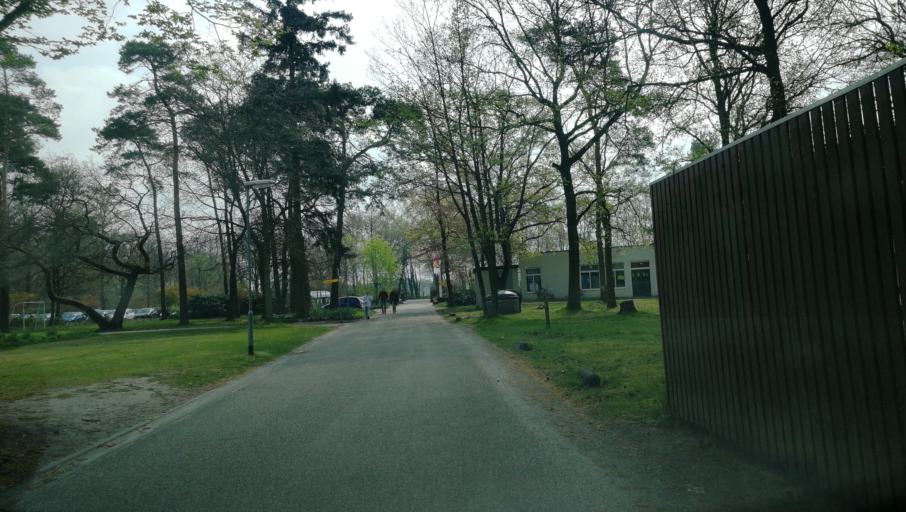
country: NL
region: Limburg
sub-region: Gemeente Venlo
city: Venlo
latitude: 51.3675
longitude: 6.1973
